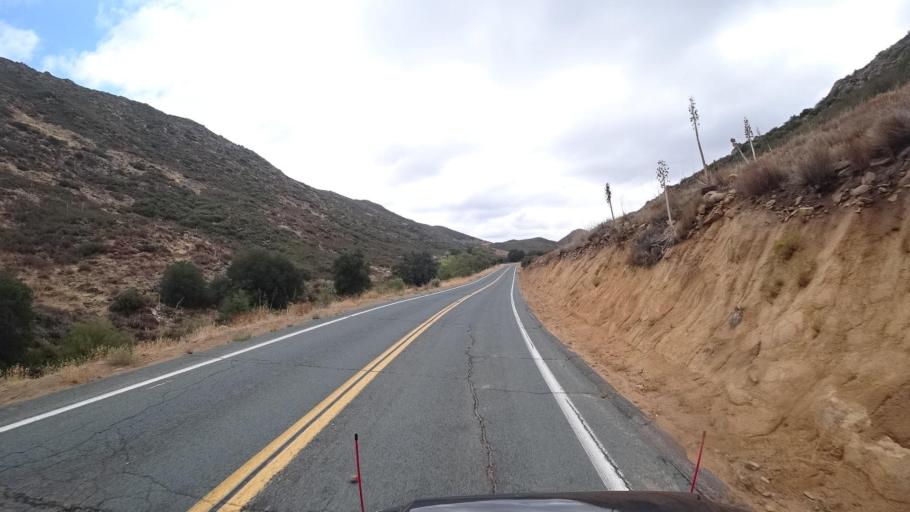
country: US
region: California
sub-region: San Diego County
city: Pine Valley
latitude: 32.7571
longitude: -116.4517
